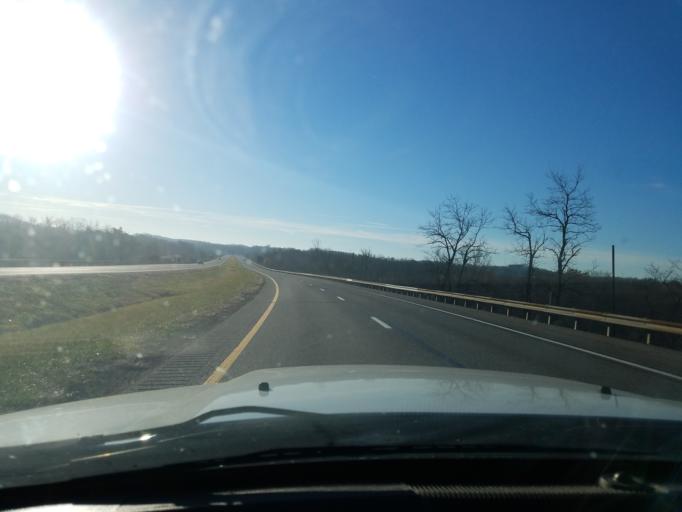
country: US
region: West Virginia
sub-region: Wood County
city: Mineral Wells
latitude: 39.2211
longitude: -81.5278
